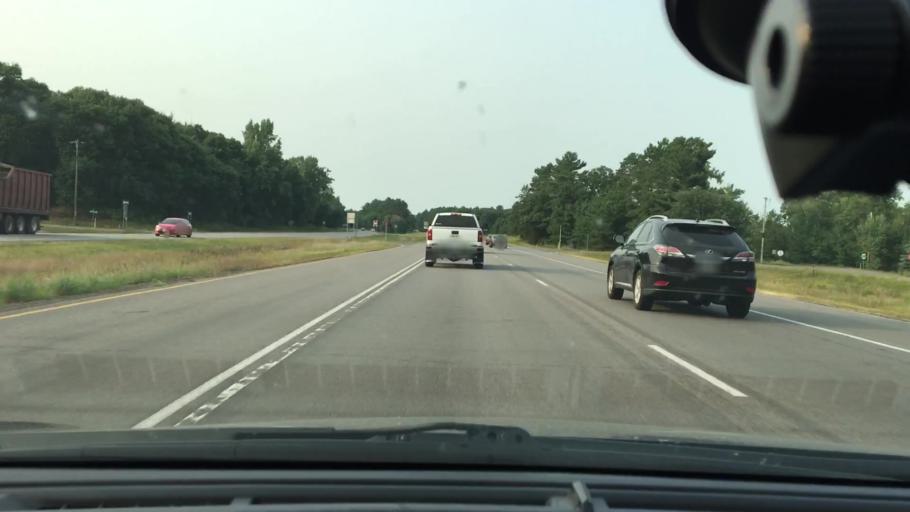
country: US
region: Minnesota
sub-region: Sherburne County
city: Zimmerman
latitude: 45.4642
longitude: -93.5835
